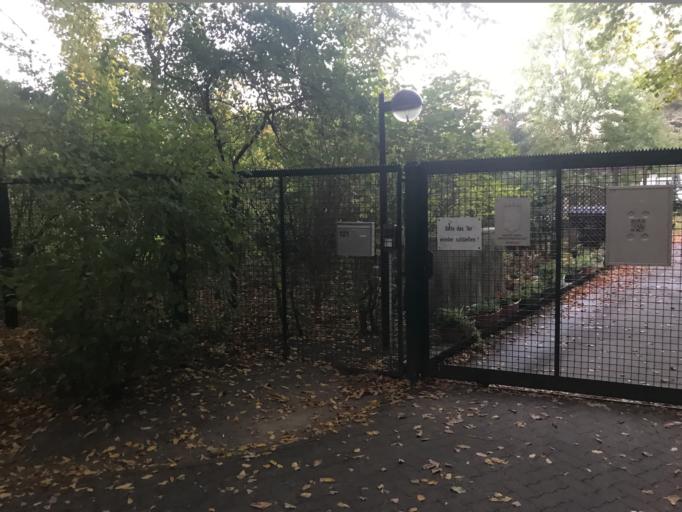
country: DE
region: Berlin
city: Britz
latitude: 52.4422
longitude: 13.4486
